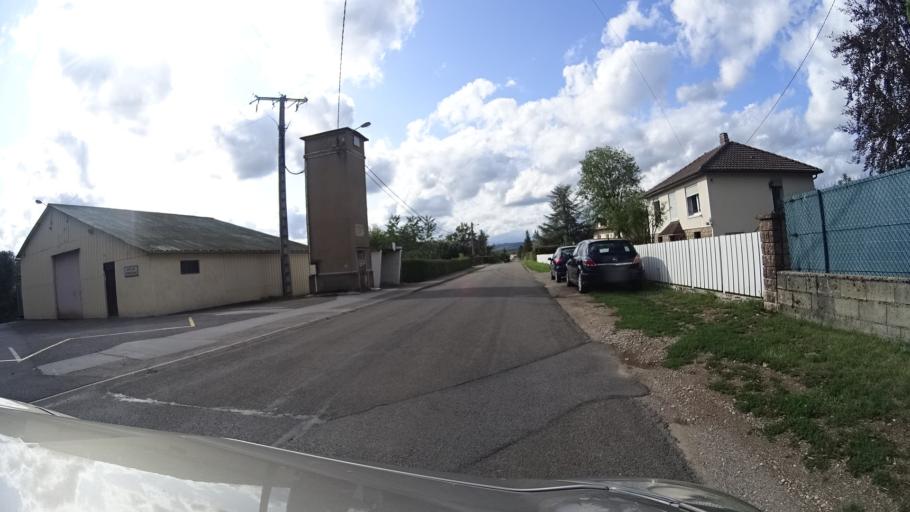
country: FR
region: Franche-Comte
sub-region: Departement du Doubs
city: Mamirolle
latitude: 47.2025
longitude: 6.1561
